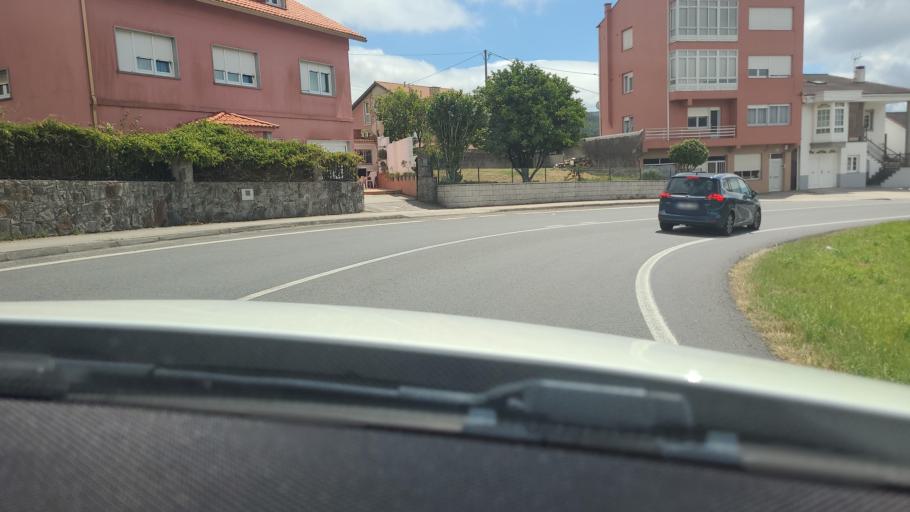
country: ES
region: Galicia
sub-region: Provincia da Coruna
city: Cee
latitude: 42.9476
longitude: -9.1797
